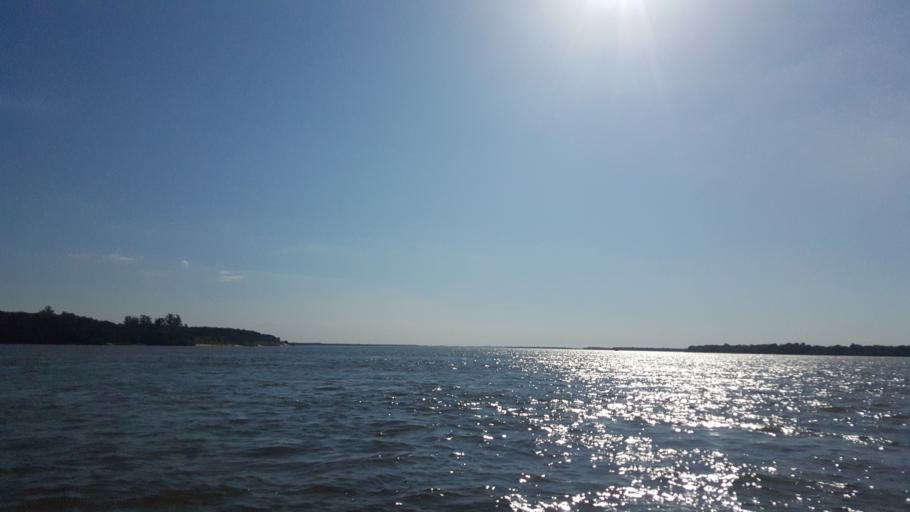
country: AR
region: Corrientes
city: Ituzaingo
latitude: -27.6029
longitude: -56.8533
